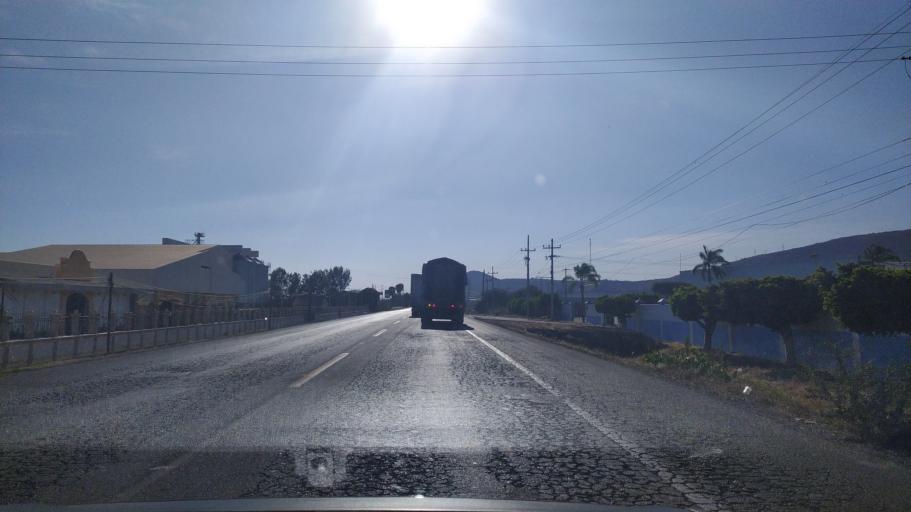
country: MX
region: Jalisco
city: Jamay
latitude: 20.2943
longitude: -102.6786
